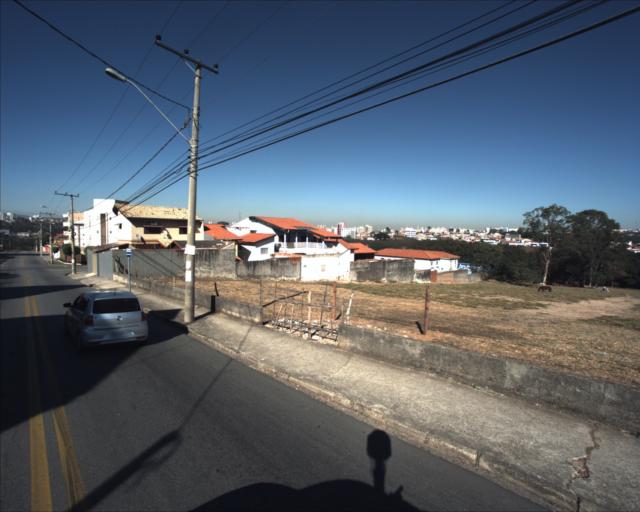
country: BR
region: Sao Paulo
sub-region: Sorocaba
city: Sorocaba
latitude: -23.4819
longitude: -47.4360
